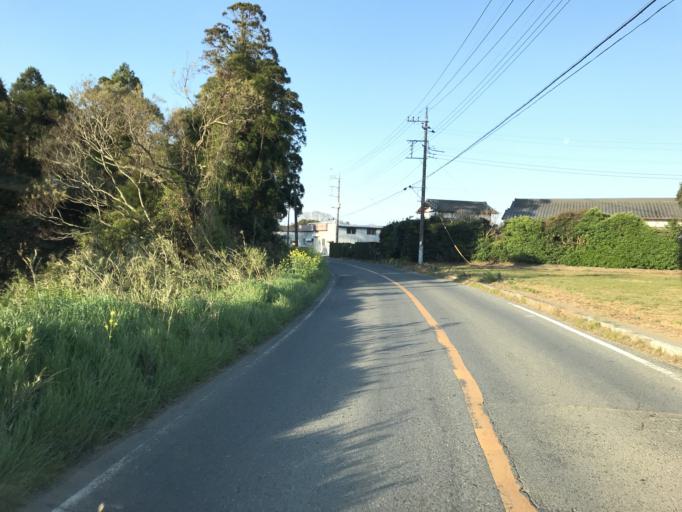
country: JP
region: Chiba
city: Yokaichiba
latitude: 35.7518
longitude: 140.5648
